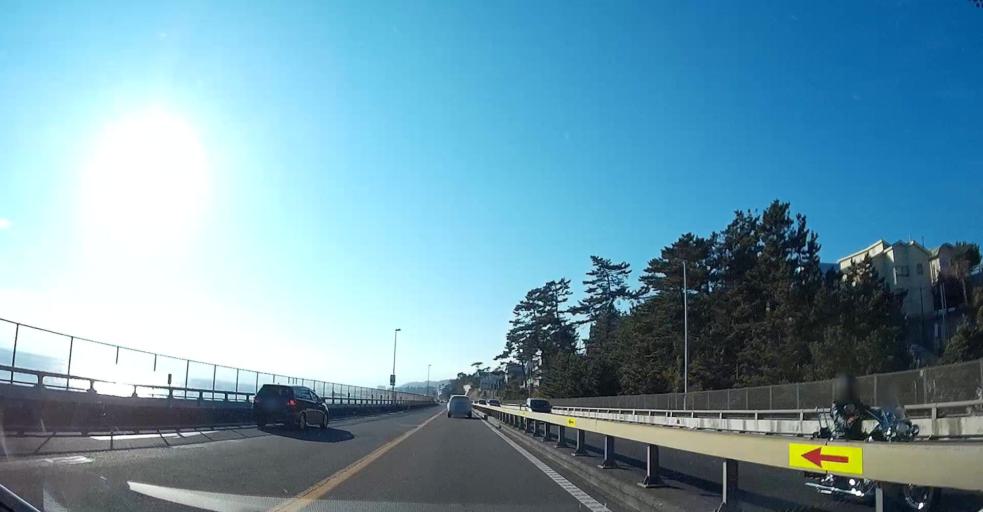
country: JP
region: Kanagawa
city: Ninomiya
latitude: 35.2964
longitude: 139.2602
